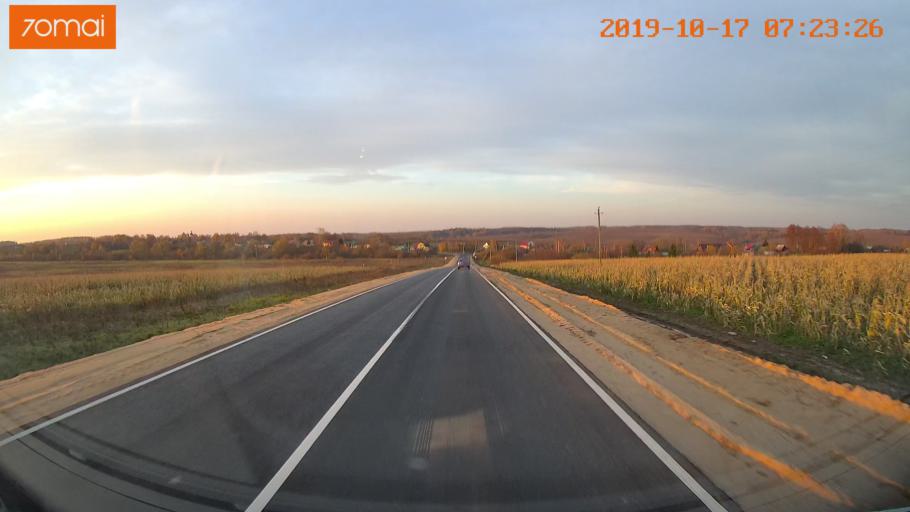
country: RU
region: Ivanovo
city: Gavrilov Posad
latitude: 56.3347
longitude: 40.1213
